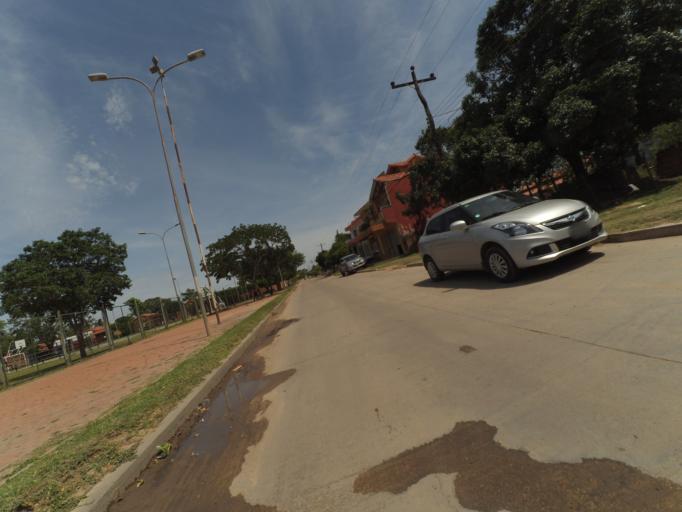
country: BO
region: Santa Cruz
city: Santa Cruz de la Sierra
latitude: -17.8316
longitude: -63.2365
